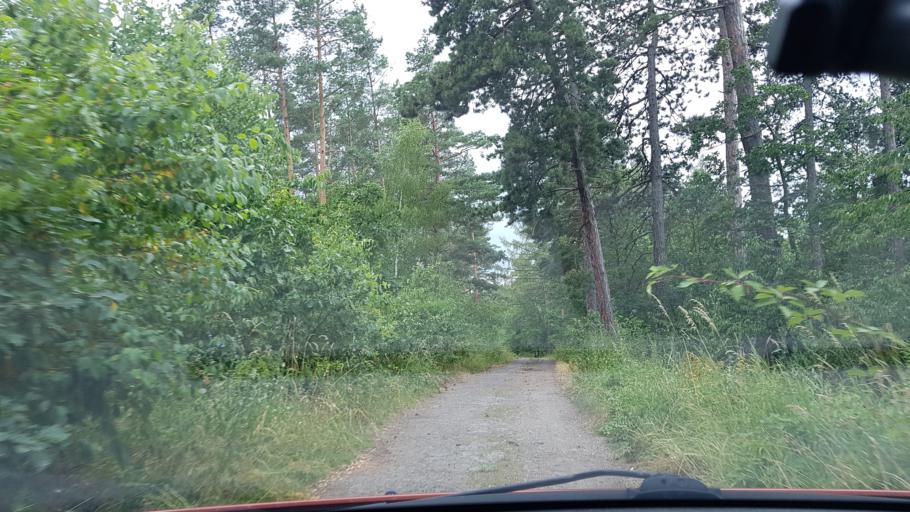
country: PL
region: Lower Silesian Voivodeship
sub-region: Powiat zabkowicki
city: Stoszowice
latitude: 50.5620
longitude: 16.7495
